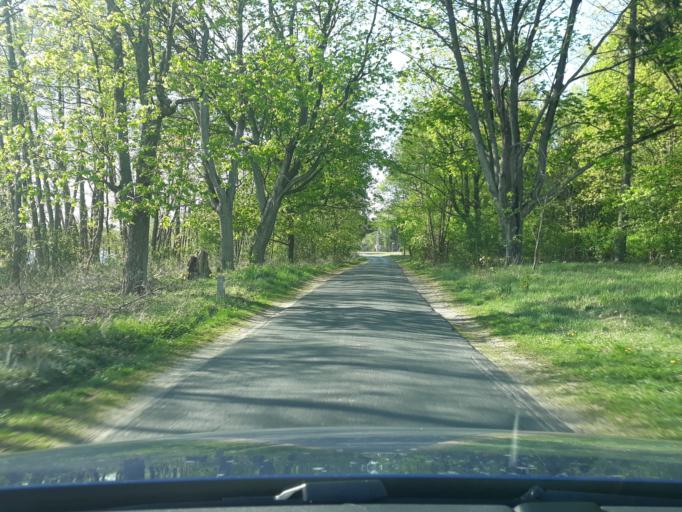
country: PL
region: Pomeranian Voivodeship
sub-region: Powiat czluchowski
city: Przechlewo
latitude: 53.8745
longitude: 17.3305
